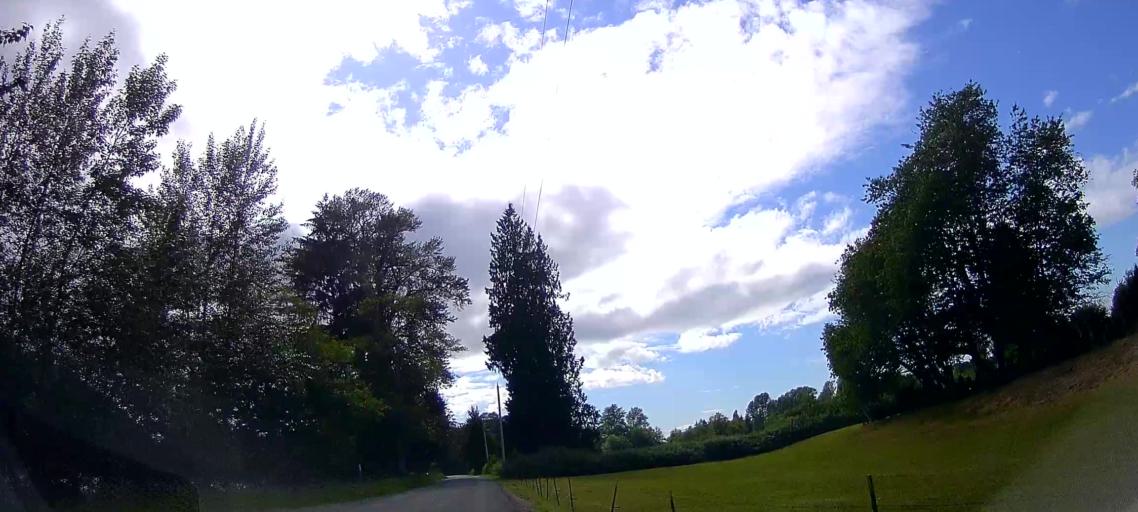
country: US
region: Washington
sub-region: Skagit County
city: Sedro-Woolley
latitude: 48.4902
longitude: -122.2141
